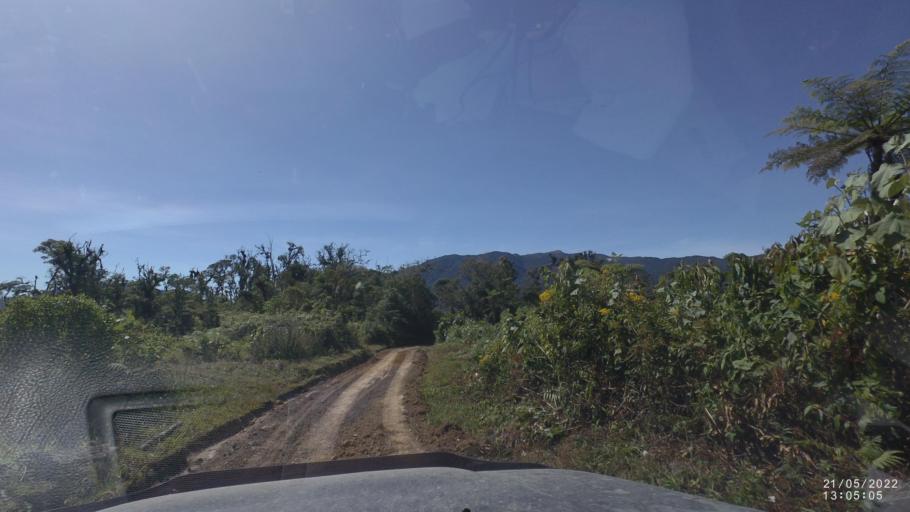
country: BO
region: Cochabamba
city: Colomi
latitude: -17.1555
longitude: -65.9493
